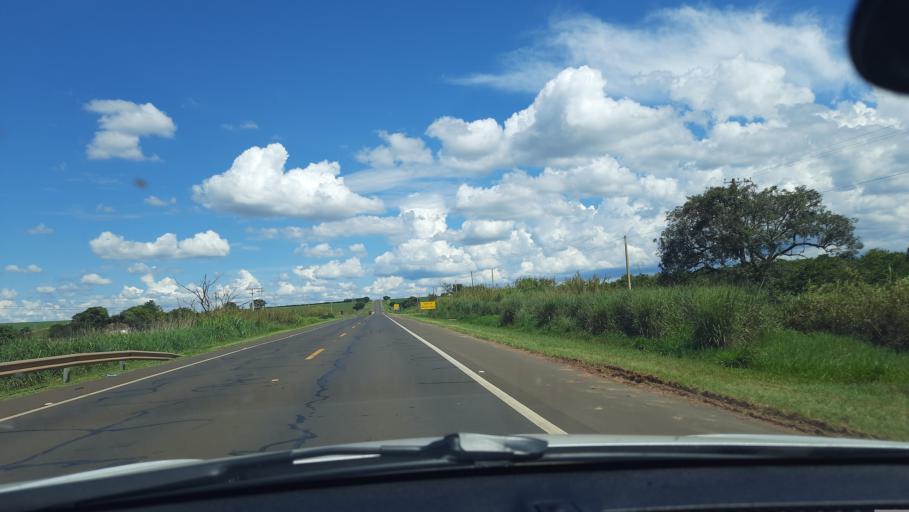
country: BR
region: Sao Paulo
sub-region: Casa Branca
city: Casa Branca
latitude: -21.8083
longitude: -47.0062
